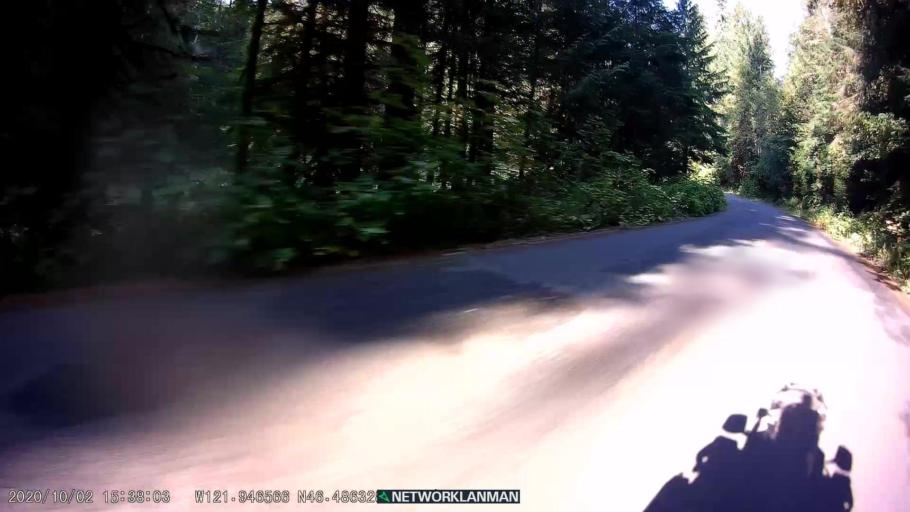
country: US
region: Washington
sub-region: Lewis County
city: Morton
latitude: 46.4865
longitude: -121.9464
